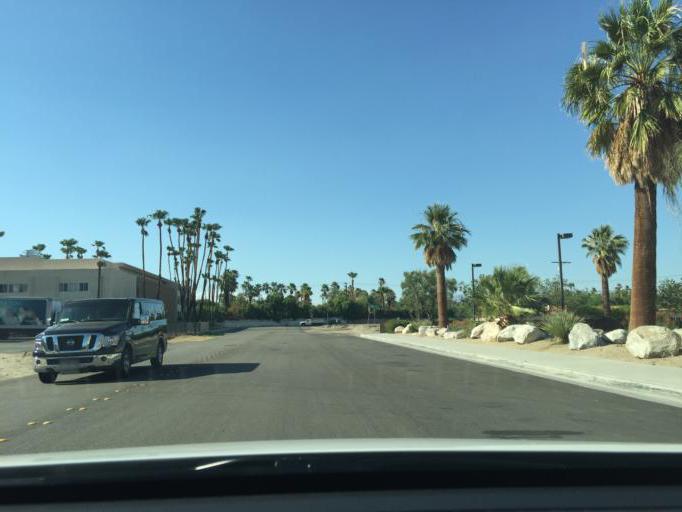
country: US
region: California
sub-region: Riverside County
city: Palm Springs
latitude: 33.8289
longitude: -116.5437
